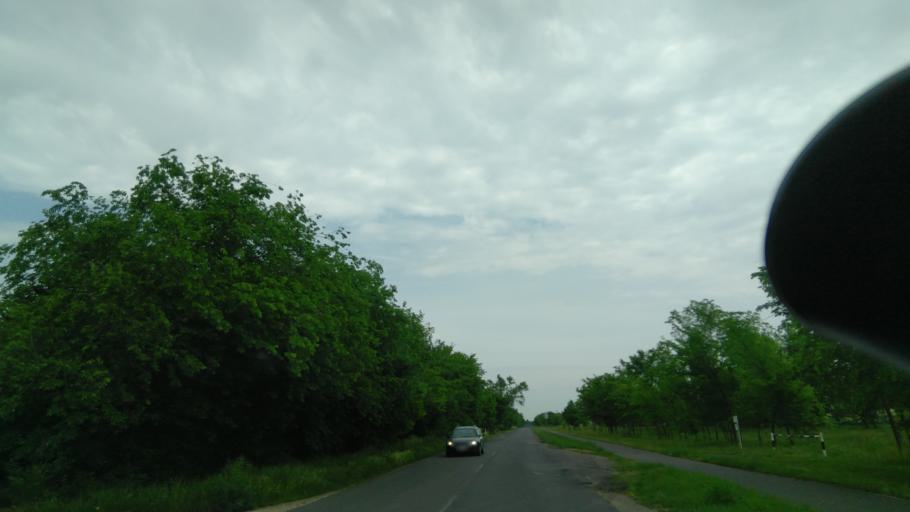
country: HU
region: Bekes
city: Szeghalom
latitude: 47.0384
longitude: 21.1835
